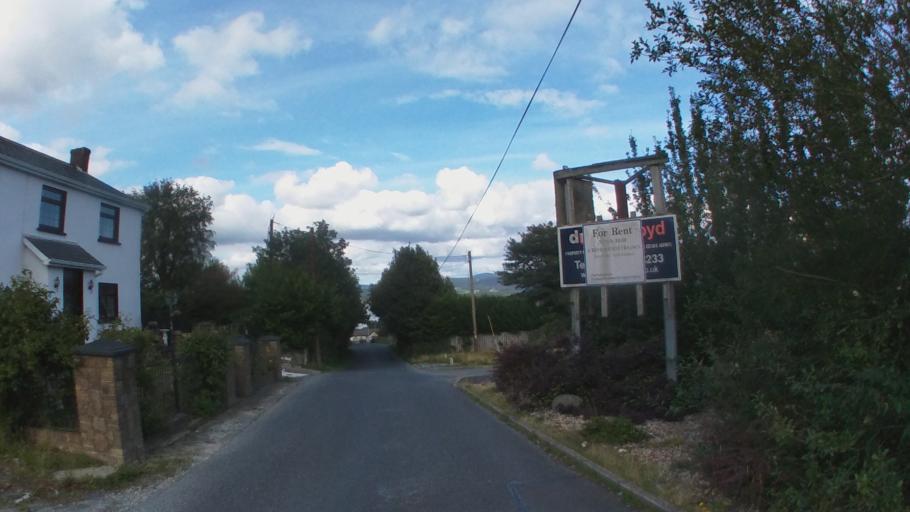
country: GB
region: Northern Ireland
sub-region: Down District
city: Warrenpoint
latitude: 54.0857
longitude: -6.2609
